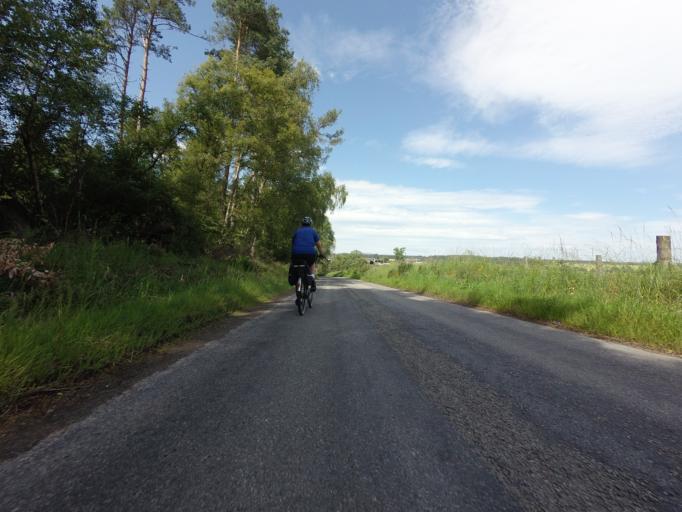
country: GB
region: Scotland
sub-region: Highland
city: Inverness
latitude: 57.5220
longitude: -4.2997
